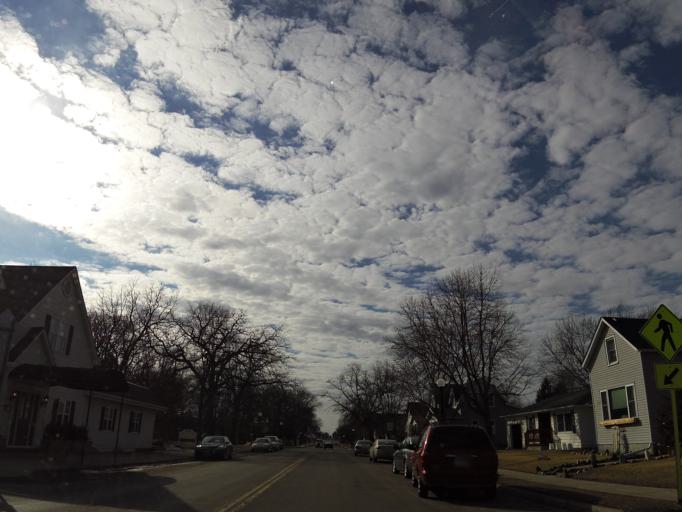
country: US
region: Minnesota
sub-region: Le Sueur County
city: New Prague
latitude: 44.5436
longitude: -93.5668
